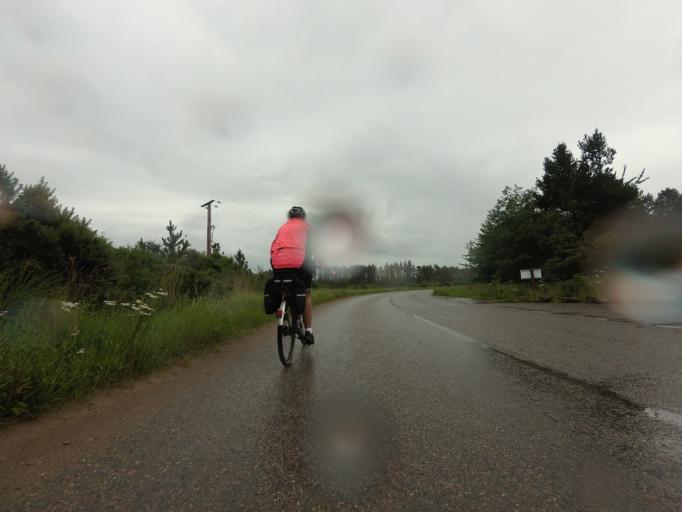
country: GB
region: Scotland
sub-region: Moray
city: Fochabers
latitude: 57.6617
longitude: -3.0600
